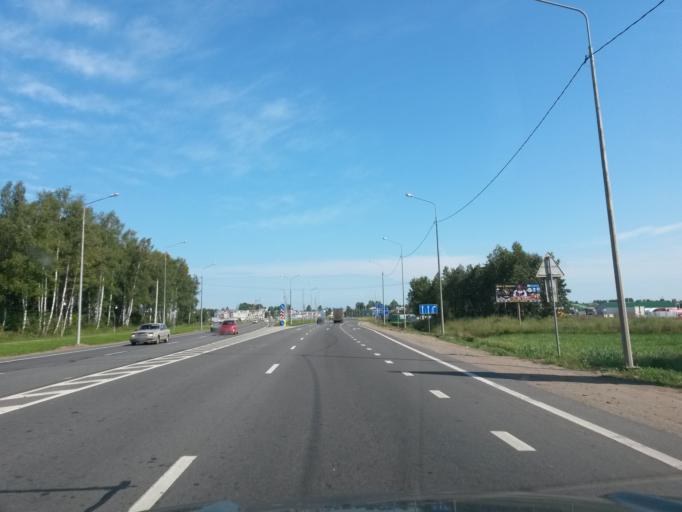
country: RU
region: Jaroslavl
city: Yaroslavl
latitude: 57.6945
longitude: 39.8989
